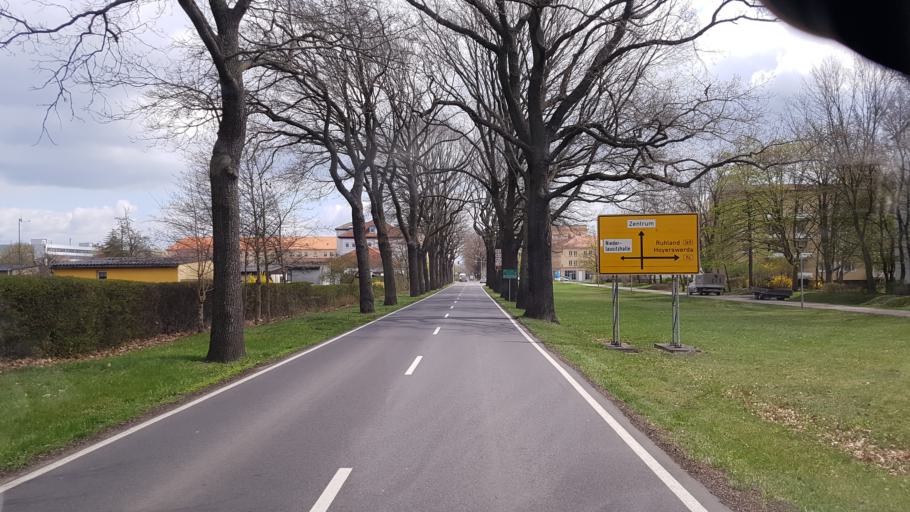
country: DE
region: Brandenburg
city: Senftenberg
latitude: 51.5235
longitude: 13.9781
